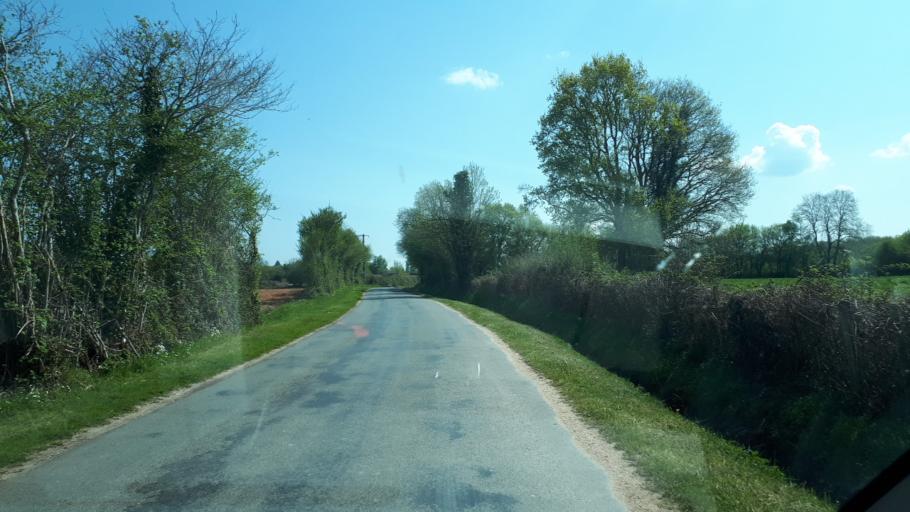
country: FR
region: Centre
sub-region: Departement du Cher
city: Neuvy-sur-Barangeon
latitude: 47.3156
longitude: 2.3533
